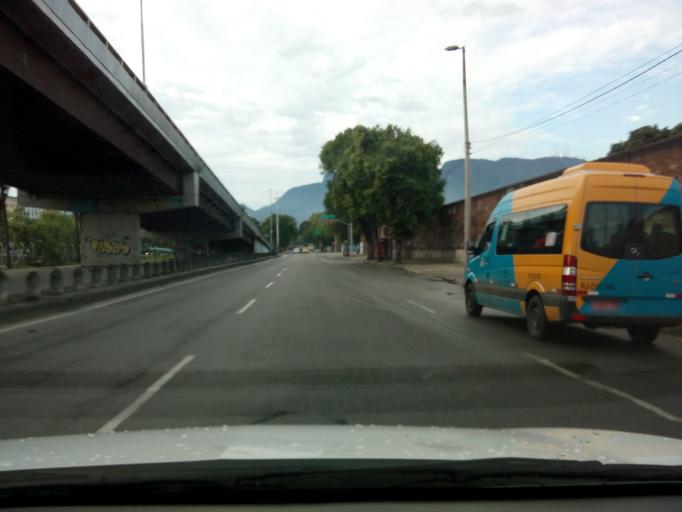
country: BR
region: Rio de Janeiro
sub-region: Rio De Janeiro
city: Rio de Janeiro
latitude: -22.9004
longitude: -43.2105
